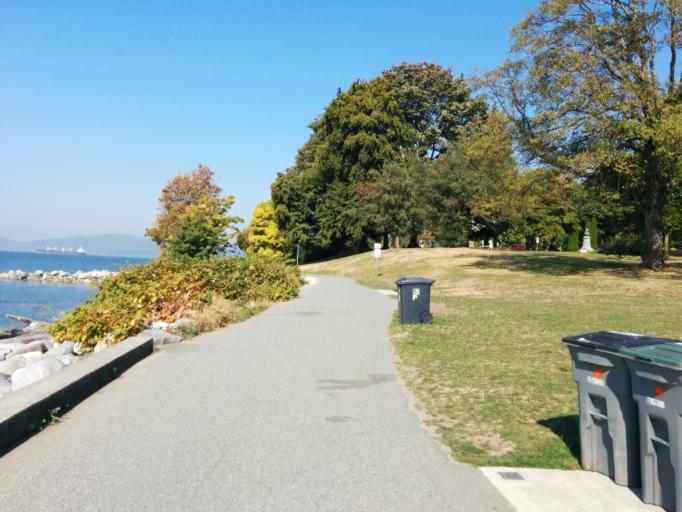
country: CA
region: British Columbia
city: West End
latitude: 49.2897
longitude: -123.1456
